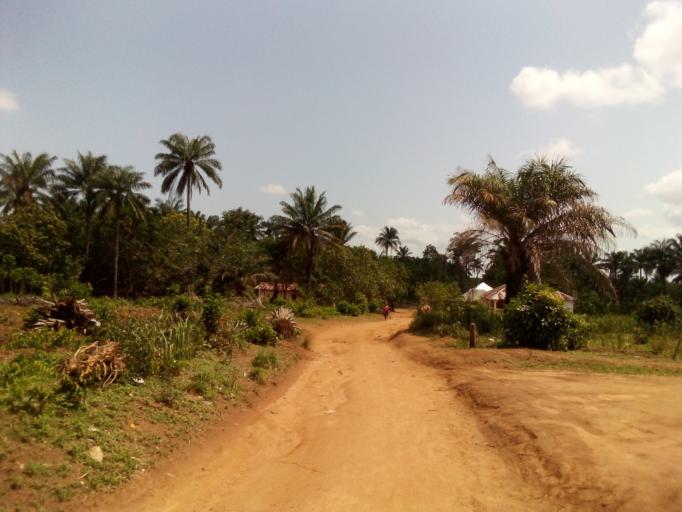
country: SL
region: Western Area
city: Waterloo
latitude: 8.3530
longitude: -13.0182
